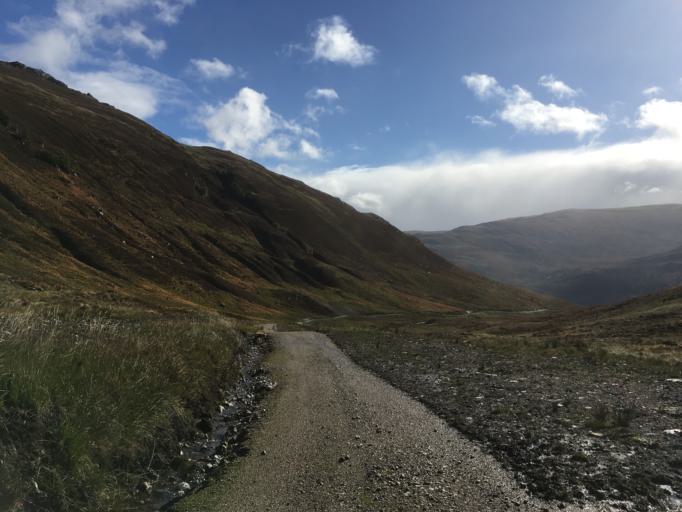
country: GB
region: Scotland
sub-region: Highland
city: Spean Bridge
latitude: 57.3523
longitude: -4.9882
